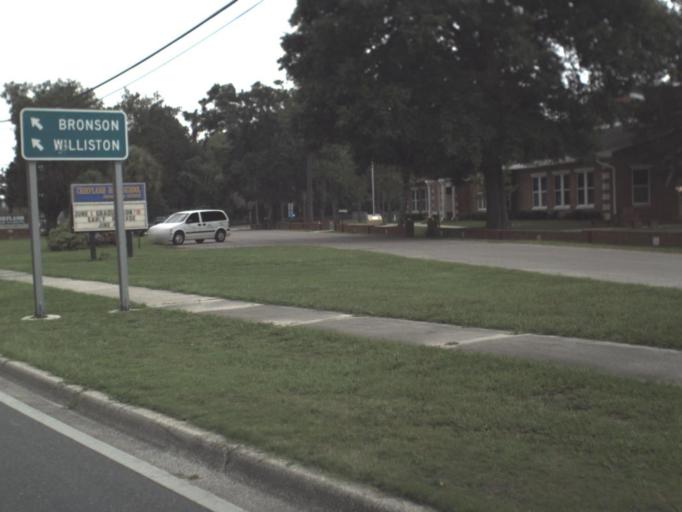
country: US
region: Florida
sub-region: Levy County
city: Chiefland
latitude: 29.4874
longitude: -82.8601
